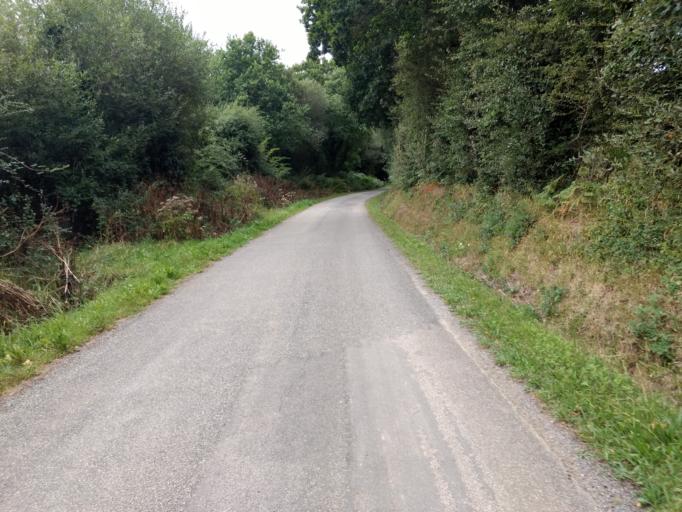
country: FR
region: Brittany
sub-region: Departement du Finistere
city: Loperhet
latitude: 48.3565
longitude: -4.2984
